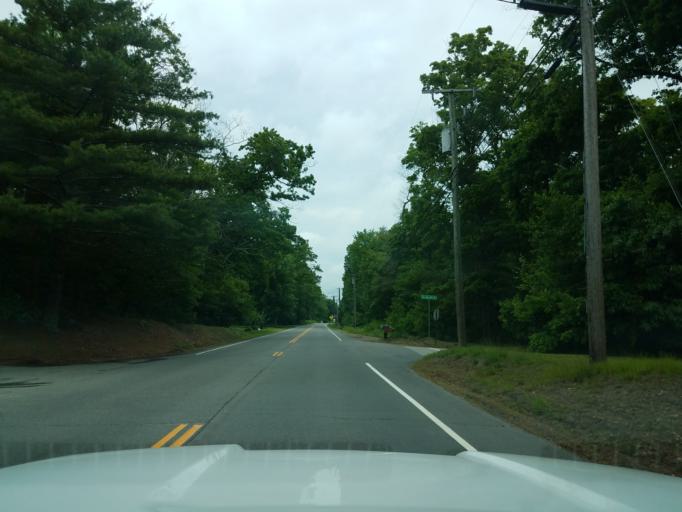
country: US
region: Connecticut
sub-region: New London County
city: Preston City
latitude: 41.5647
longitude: -71.8686
